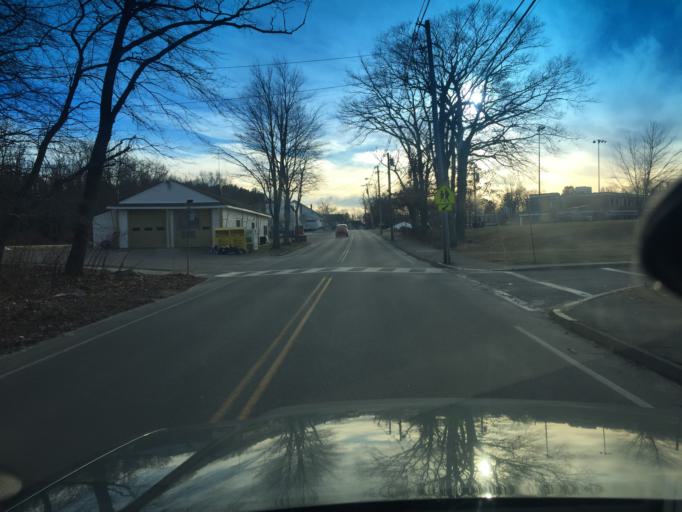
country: US
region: Massachusetts
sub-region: Middlesex County
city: Holliston
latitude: 42.2058
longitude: -71.4207
